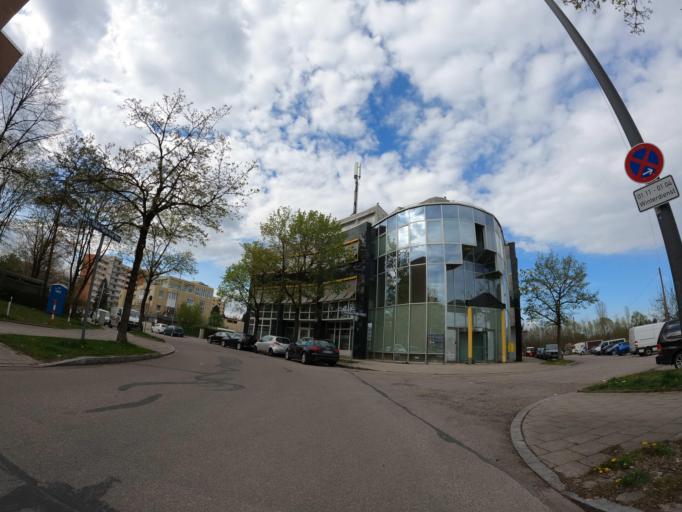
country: DE
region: Bavaria
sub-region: Upper Bavaria
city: Neubiberg
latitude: 48.0977
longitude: 11.6613
